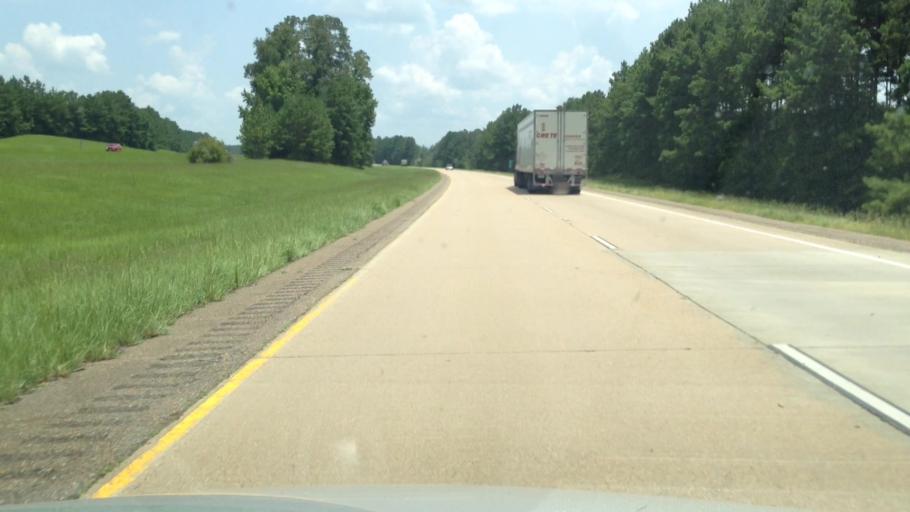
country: US
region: Louisiana
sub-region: Rapides Parish
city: Lecompte
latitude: 31.0373
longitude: -92.4144
